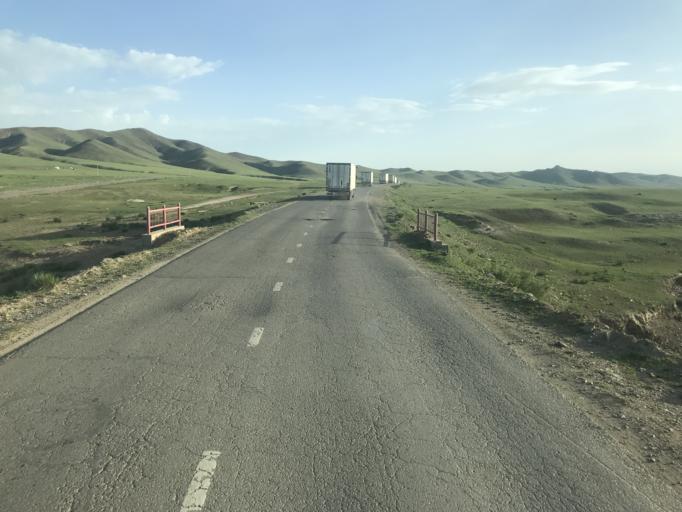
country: MN
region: Central Aimak
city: Bornuur
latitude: 48.4294
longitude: 106.1933
